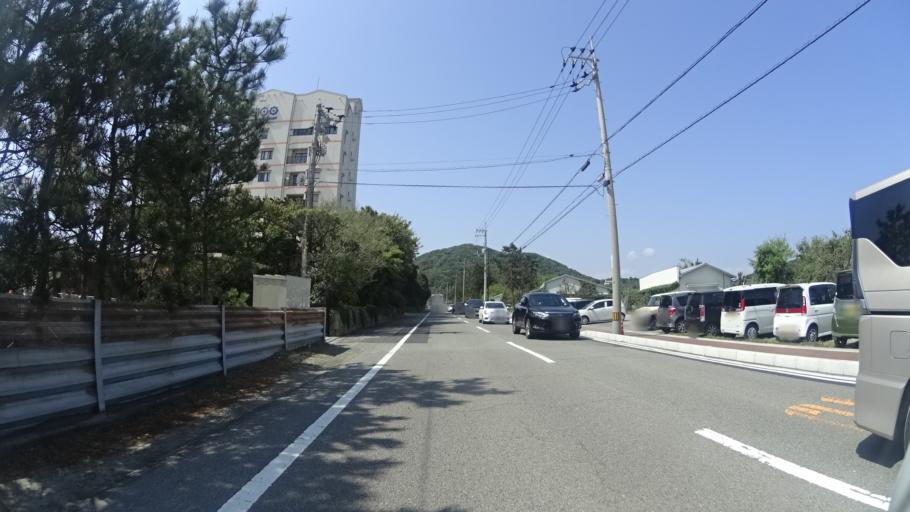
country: JP
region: Tokushima
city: Narutocho-mitsuishi
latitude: 34.2213
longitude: 134.6337
